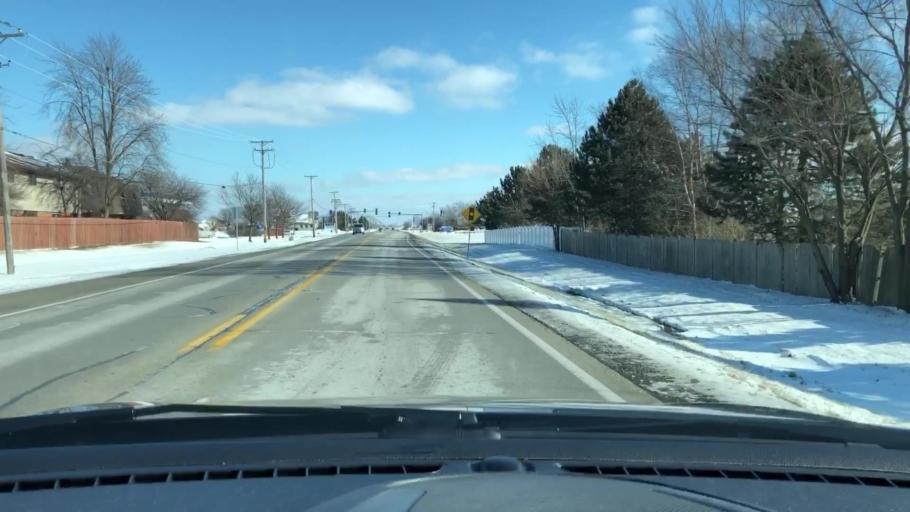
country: US
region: Illinois
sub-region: Will County
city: New Lenox
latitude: 41.4827
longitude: -87.9874
